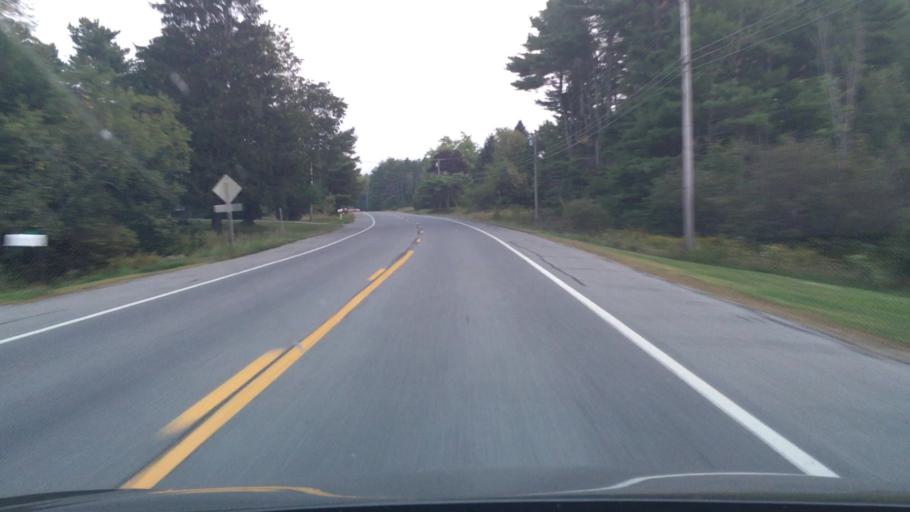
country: US
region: Maine
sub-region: Waldo County
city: Stockton Springs
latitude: 44.5490
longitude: -68.8644
